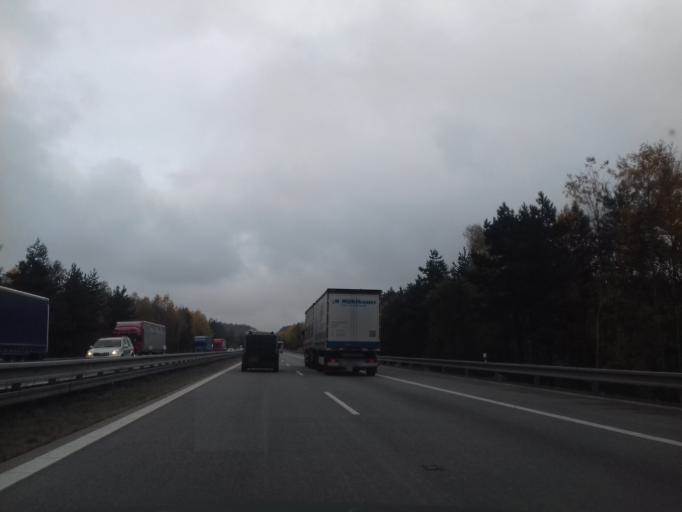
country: CZ
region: Central Bohemia
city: Cechtice
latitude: 49.6170
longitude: 15.1361
